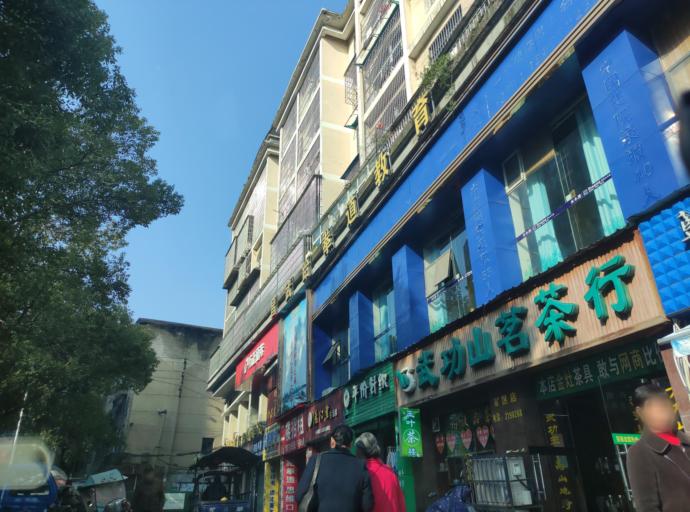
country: CN
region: Jiangxi Sheng
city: Pingxiang
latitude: 27.6339
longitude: 113.8424
